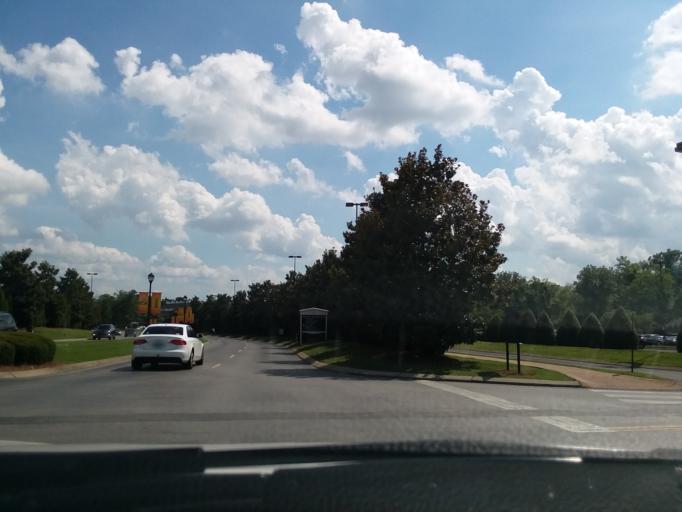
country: US
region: Tennessee
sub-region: Davidson County
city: Lakewood
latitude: 36.2146
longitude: -86.6977
